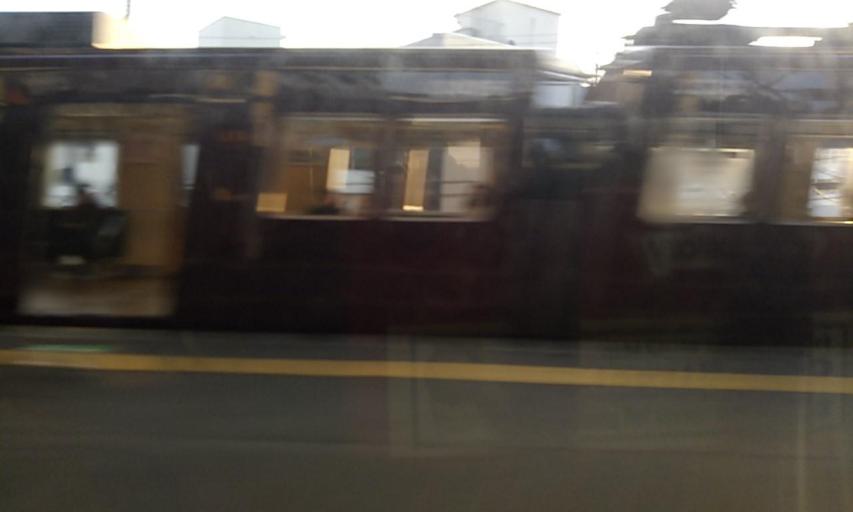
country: JP
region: Osaka
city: Suita
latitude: 34.7571
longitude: 135.5335
